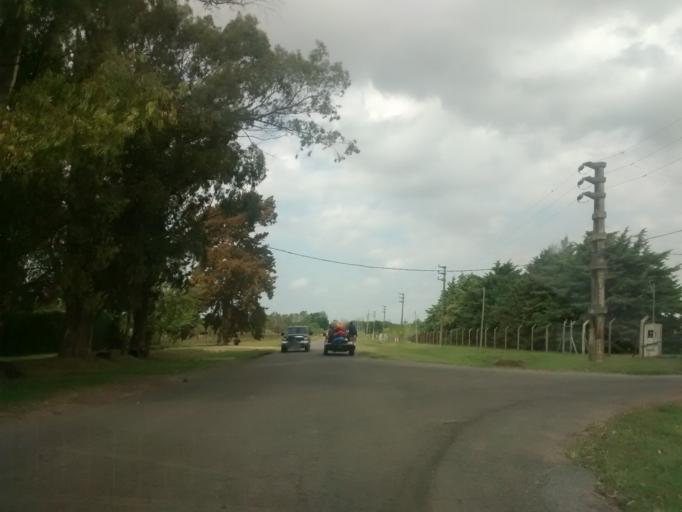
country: AR
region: Buenos Aires
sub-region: Partido de La Plata
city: La Plata
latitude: -34.9992
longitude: -57.9056
